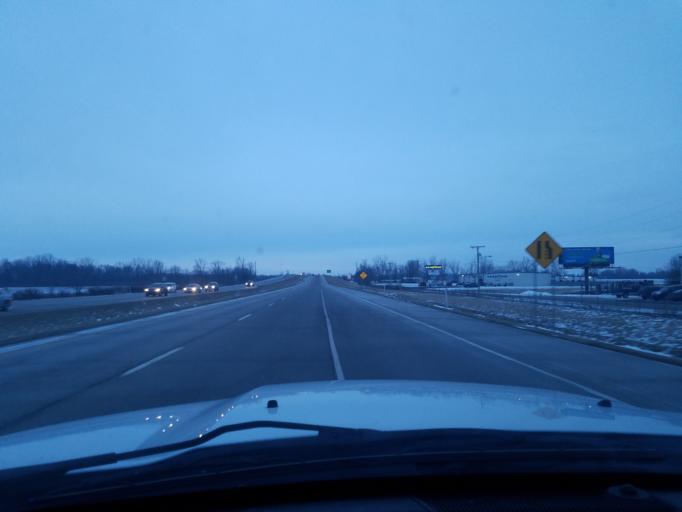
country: US
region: Indiana
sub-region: Delaware County
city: Muncie
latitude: 40.2179
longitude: -85.3405
